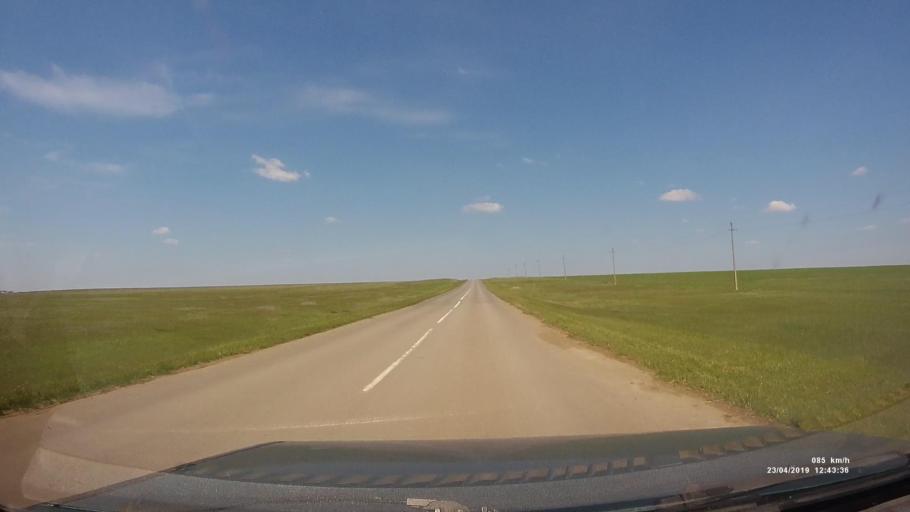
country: RU
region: Kalmykiya
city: Yashalta
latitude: 46.4660
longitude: 42.6502
